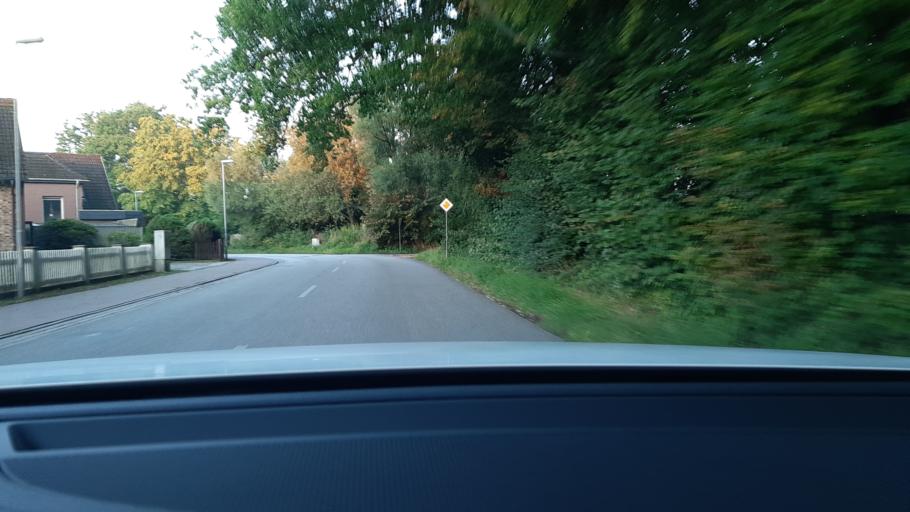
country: DE
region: Schleswig-Holstein
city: Hamberge
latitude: 53.8298
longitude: 10.6056
